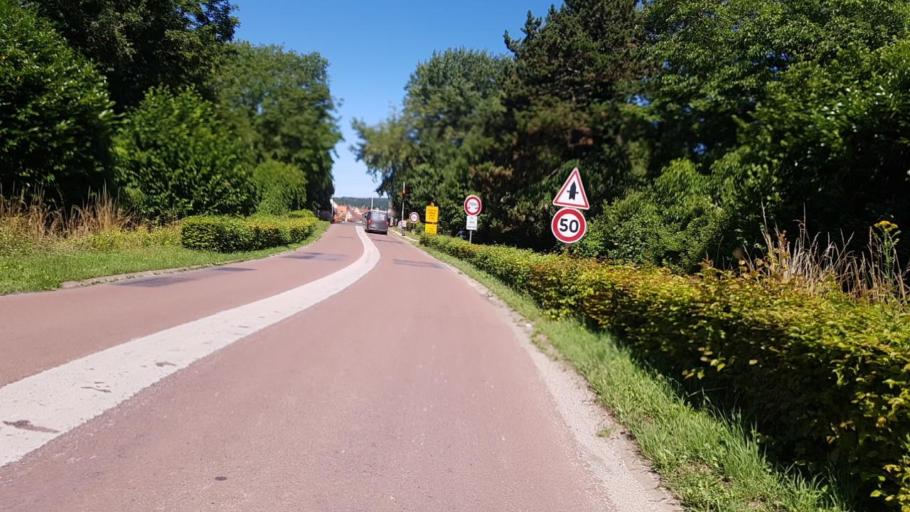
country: FR
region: Ile-de-France
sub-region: Departement de Seine-et-Marne
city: Saacy-sur-Marne
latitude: 48.9703
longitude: 3.1928
